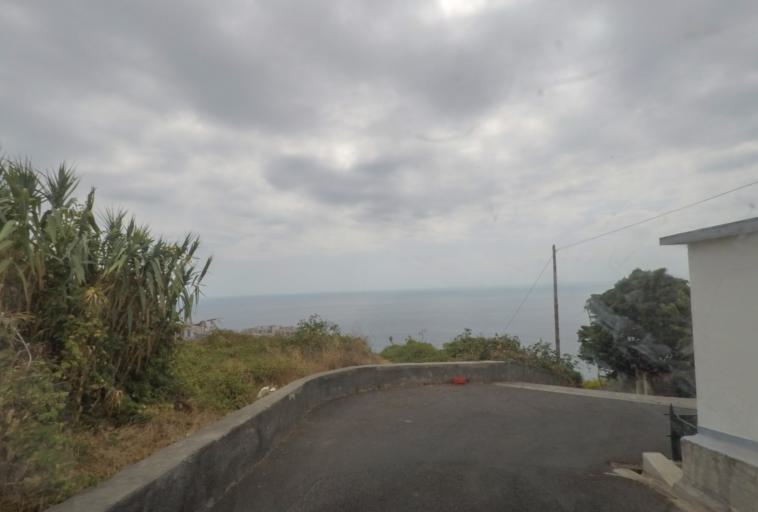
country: PT
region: Madeira
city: Camara de Lobos
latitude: 32.6466
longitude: -16.9497
